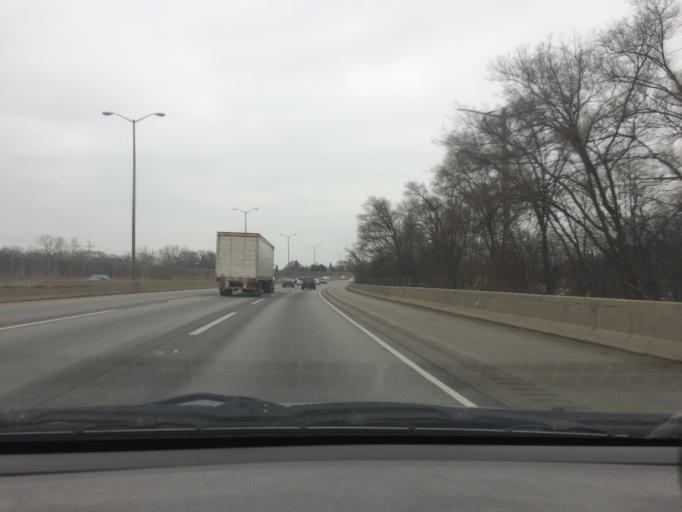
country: US
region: Illinois
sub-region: DuPage County
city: Lombard
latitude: 41.8791
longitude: -88.0330
